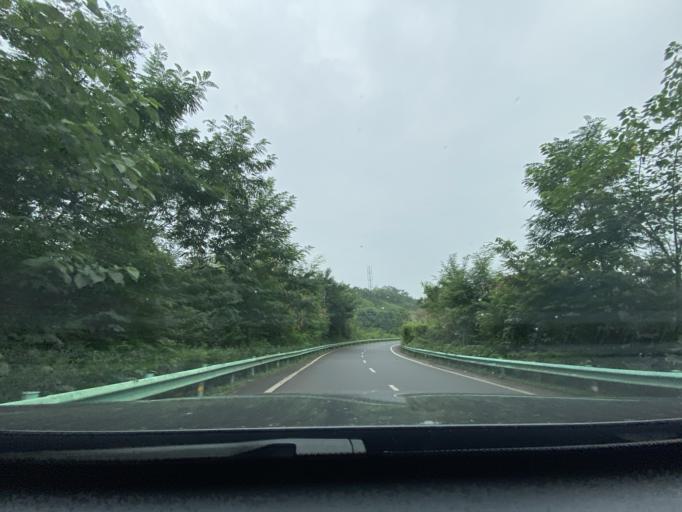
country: CN
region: Sichuan
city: Wenlin
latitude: 30.2974
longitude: 104.1237
